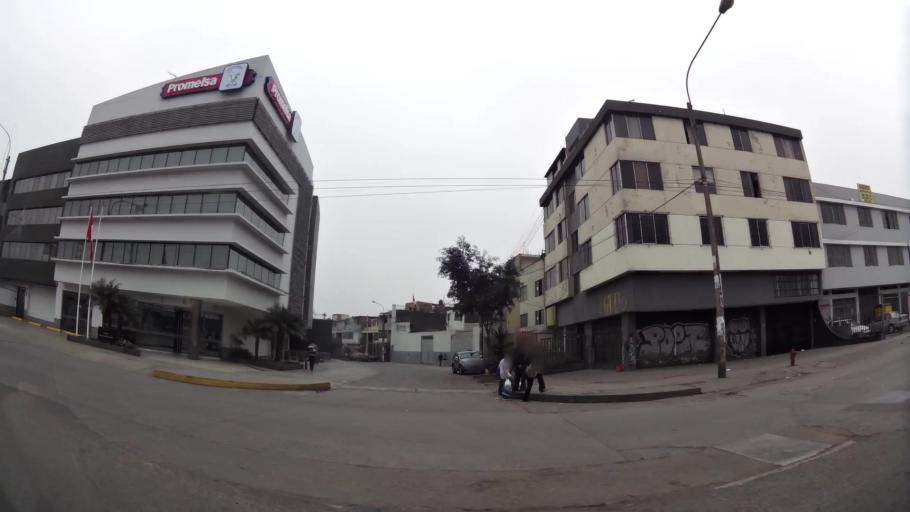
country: PE
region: Lima
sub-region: Lima
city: San Luis
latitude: -12.0800
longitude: -77.0126
